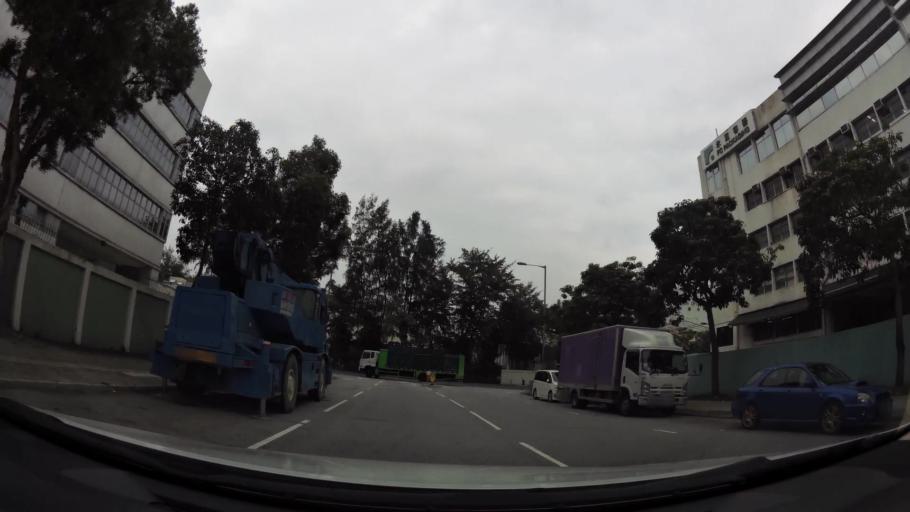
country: HK
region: Tai Po
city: Tai Po
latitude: 22.4613
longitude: 114.1879
